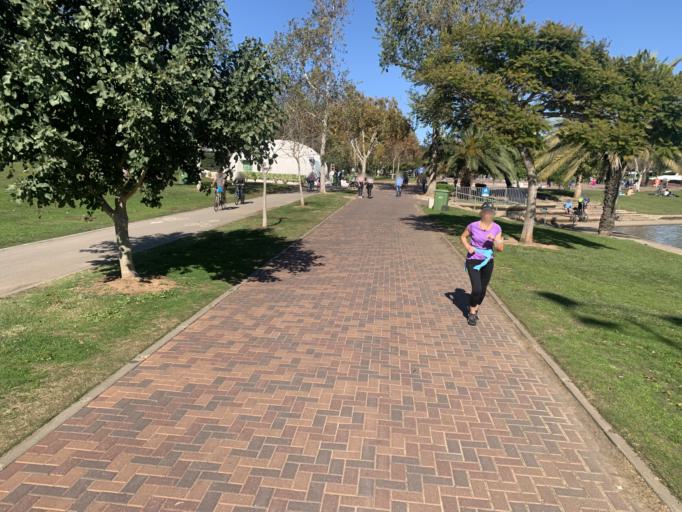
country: IL
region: Tel Aviv
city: Ramat Gan
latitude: 32.0978
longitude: 34.8092
